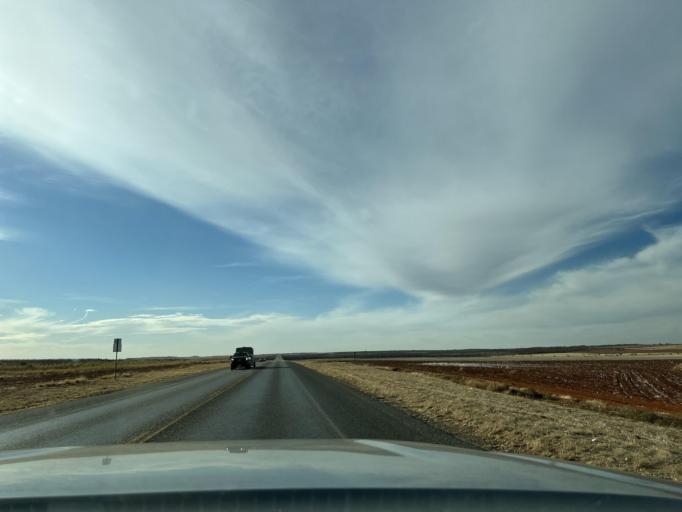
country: US
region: Texas
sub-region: Fisher County
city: Rotan
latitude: 32.7404
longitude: -100.4961
